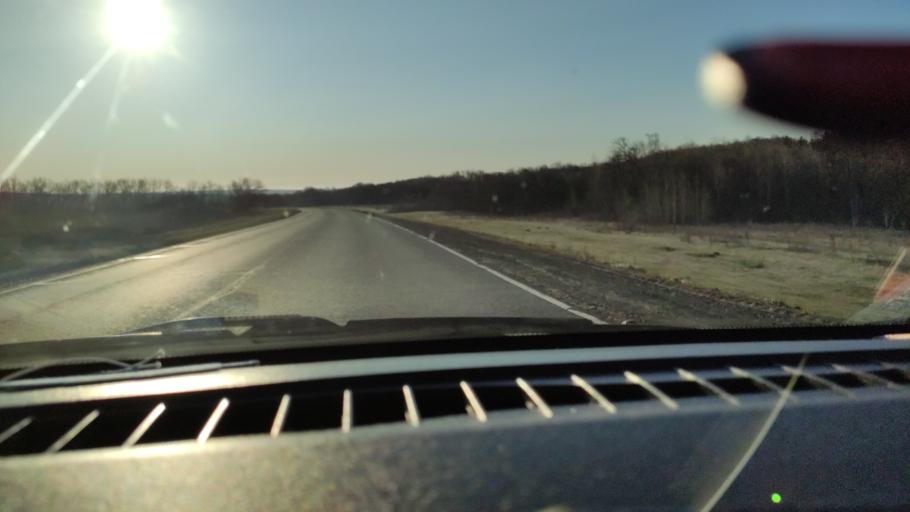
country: RU
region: Saratov
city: Tersa
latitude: 52.1024
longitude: 47.4564
